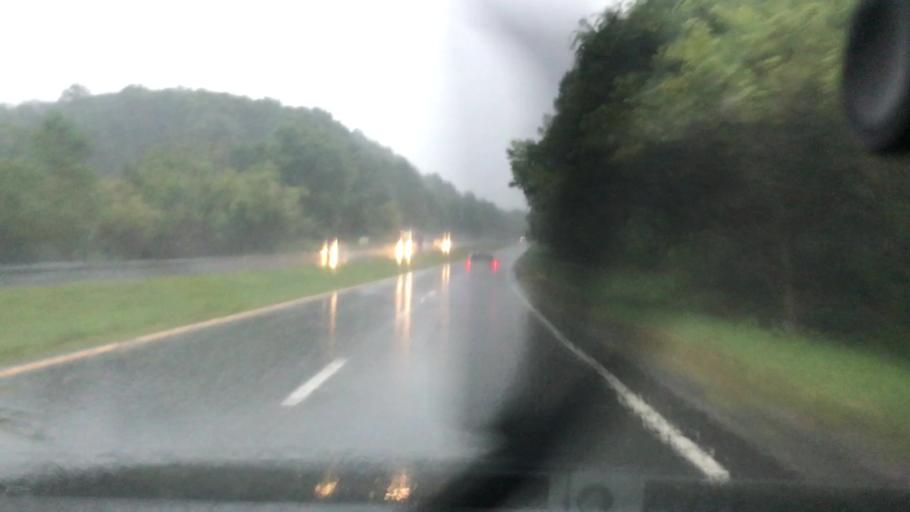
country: US
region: Virginia
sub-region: Giles County
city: Pearisburg
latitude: 37.3390
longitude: -80.7178
